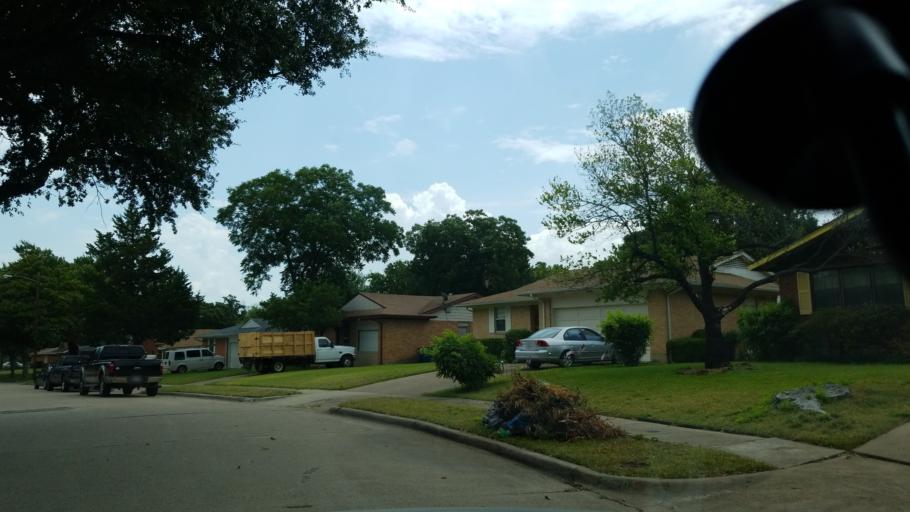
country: US
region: Texas
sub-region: Dallas County
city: Cockrell Hill
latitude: 32.6876
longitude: -96.8532
